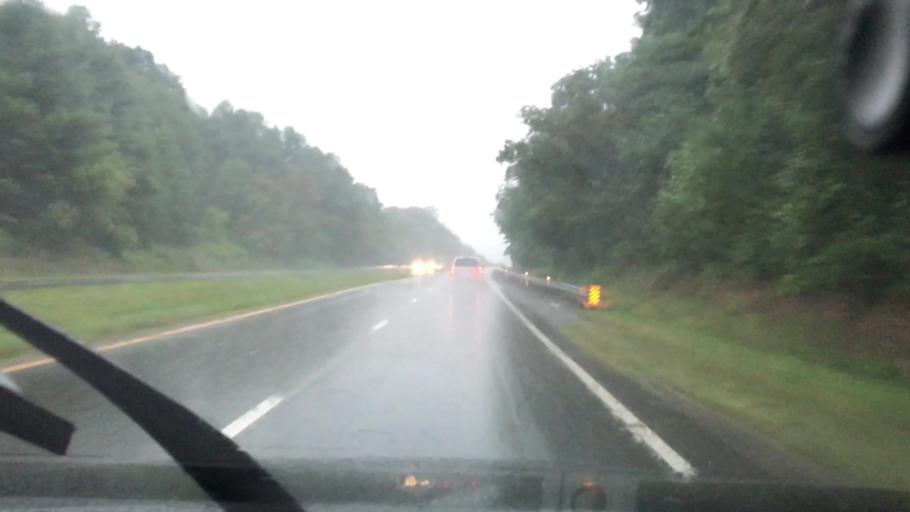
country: US
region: Virginia
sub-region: Giles County
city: Pearisburg
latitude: 37.3383
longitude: -80.7132
